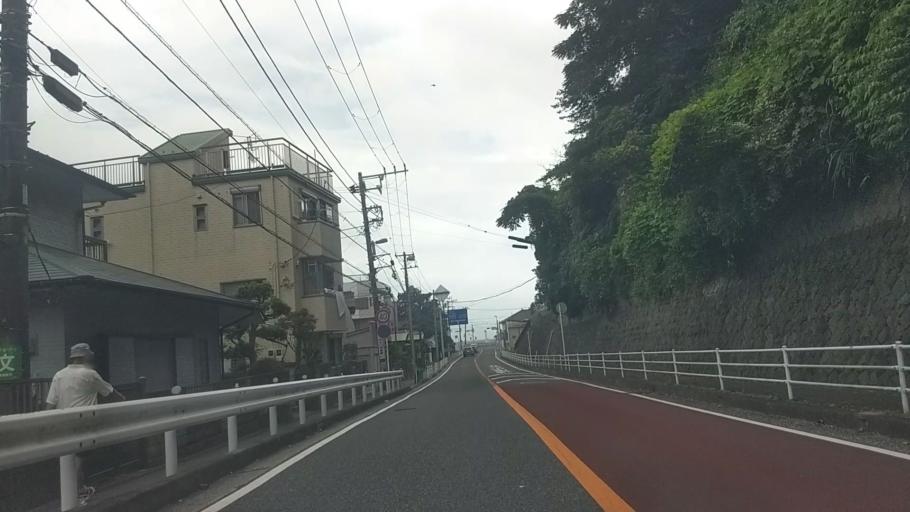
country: JP
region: Kanagawa
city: Yokosuka
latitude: 35.2501
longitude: 139.7327
